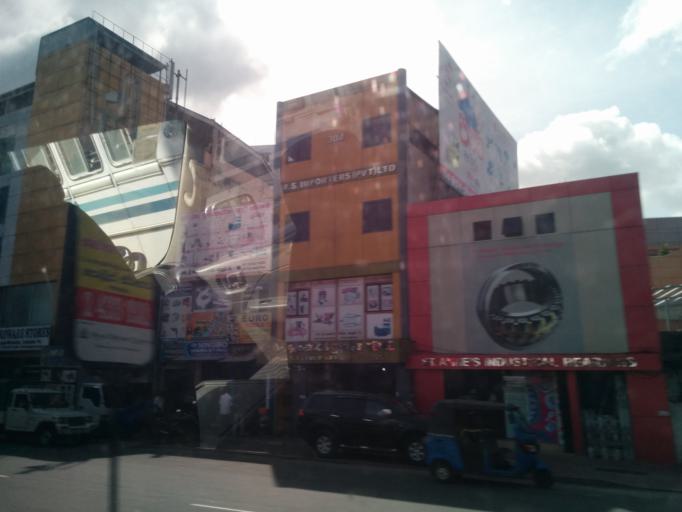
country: LK
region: Western
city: Colombo
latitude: 6.9348
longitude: 79.8661
